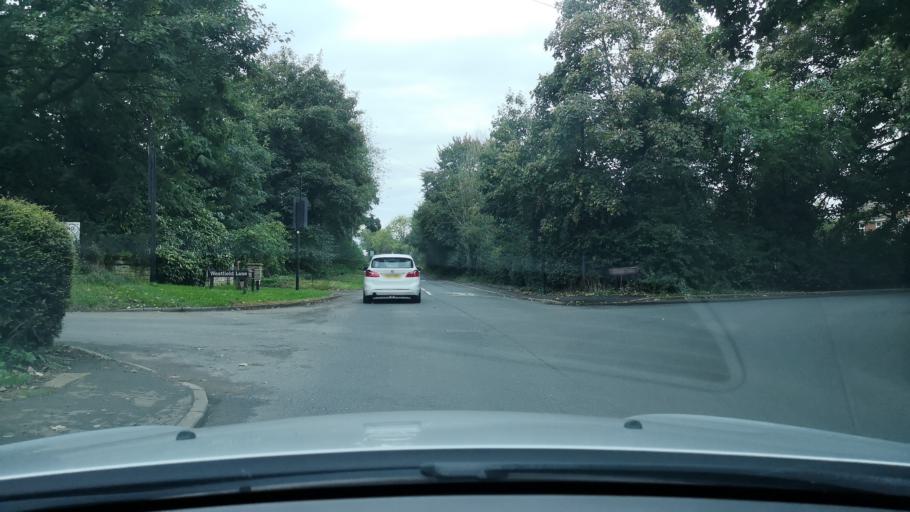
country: GB
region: England
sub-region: City and Borough of Wakefield
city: Darrington
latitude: 53.6752
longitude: -1.2741
